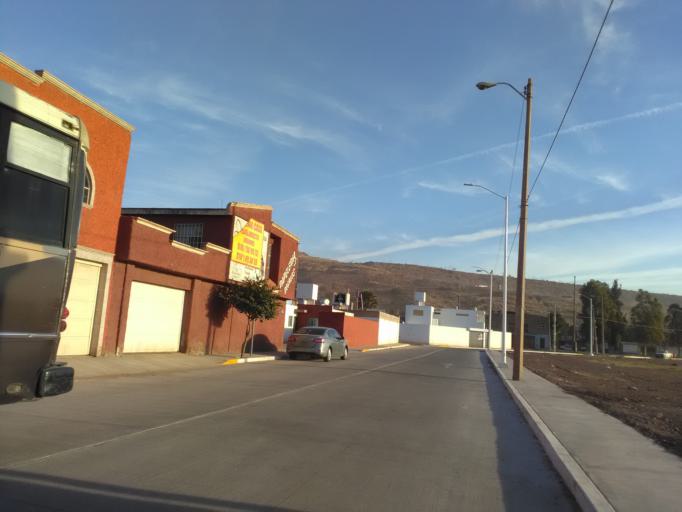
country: MX
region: Durango
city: Victoria de Durango
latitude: 24.0471
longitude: -104.6654
